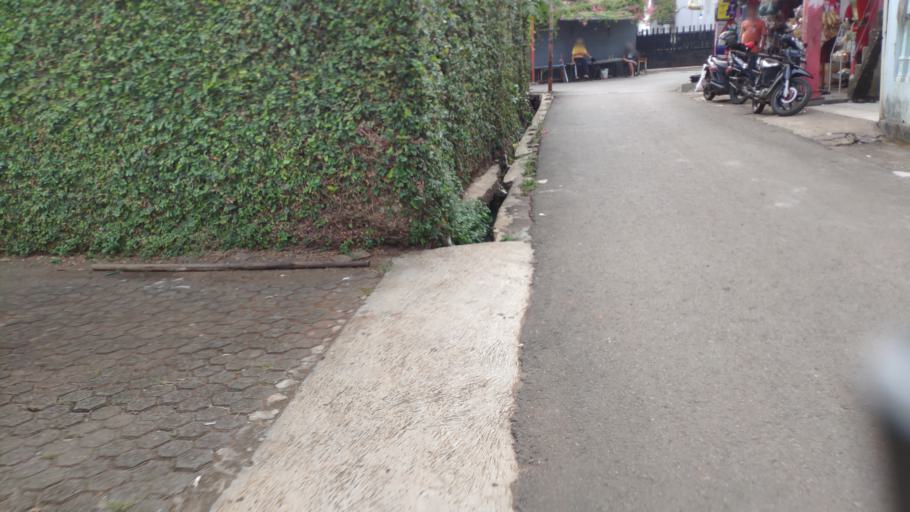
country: ID
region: West Java
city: Pamulang
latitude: -6.3142
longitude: 106.8059
